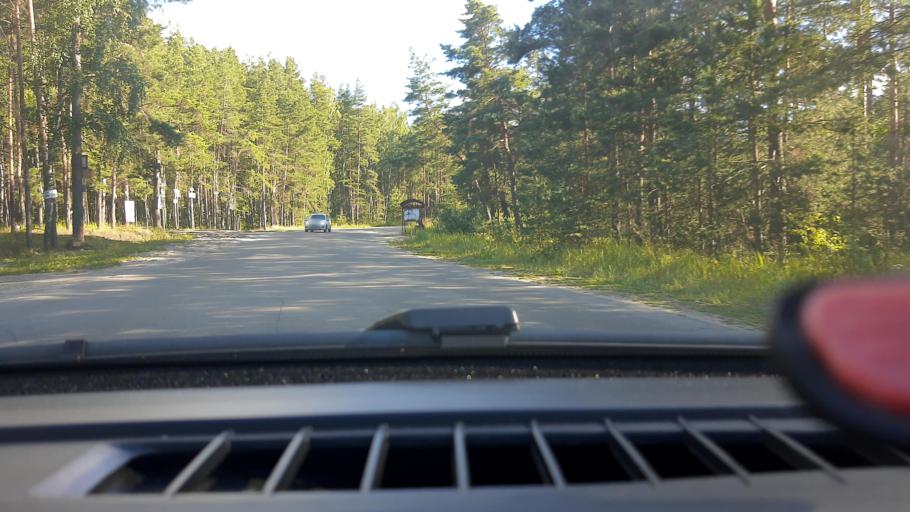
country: RU
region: Nizjnij Novgorod
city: Babino
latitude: 56.3250
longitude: 43.6342
